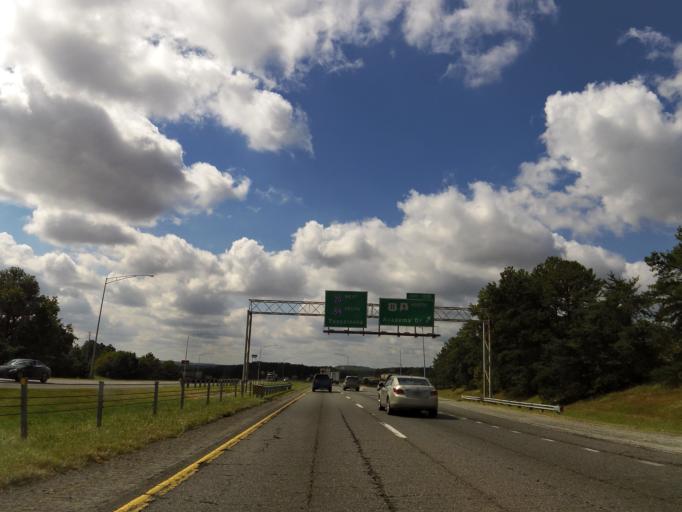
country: US
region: Alabama
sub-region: Jefferson County
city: Bessemer
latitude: 33.3697
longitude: -86.9983
